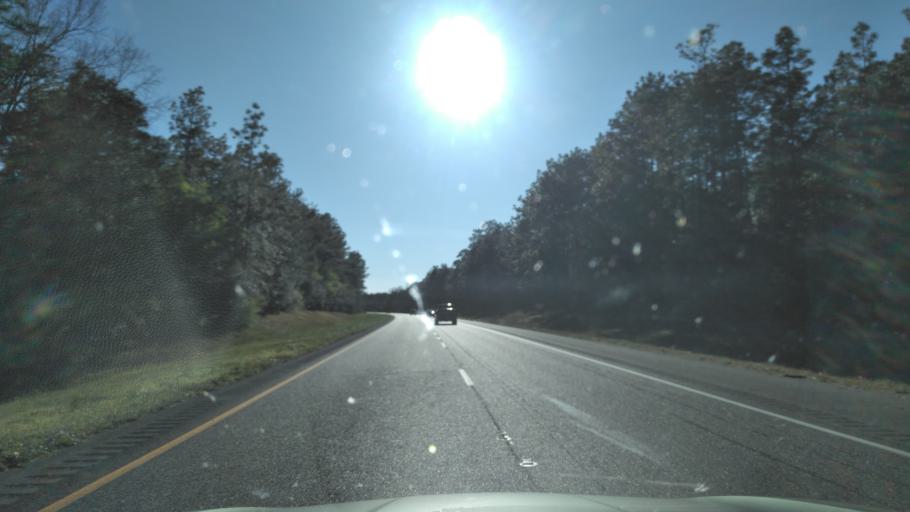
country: US
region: Alabama
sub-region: Escambia County
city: Atmore
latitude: 31.0614
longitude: -87.5759
